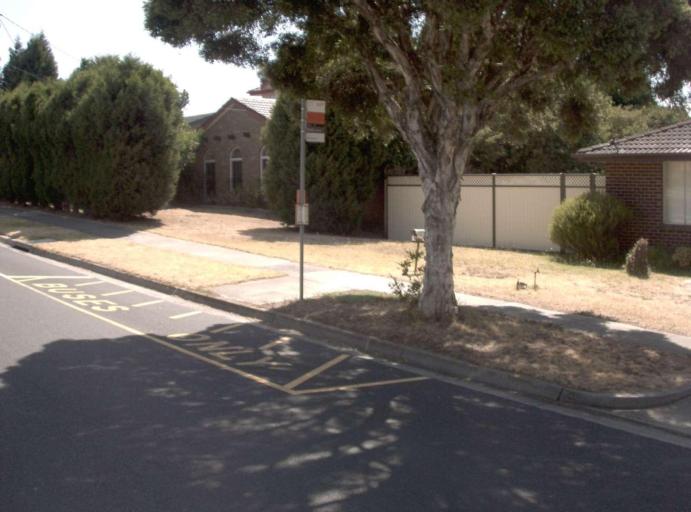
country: AU
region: Victoria
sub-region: Greater Dandenong
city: Noble Park North
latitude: -37.9524
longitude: 145.1912
